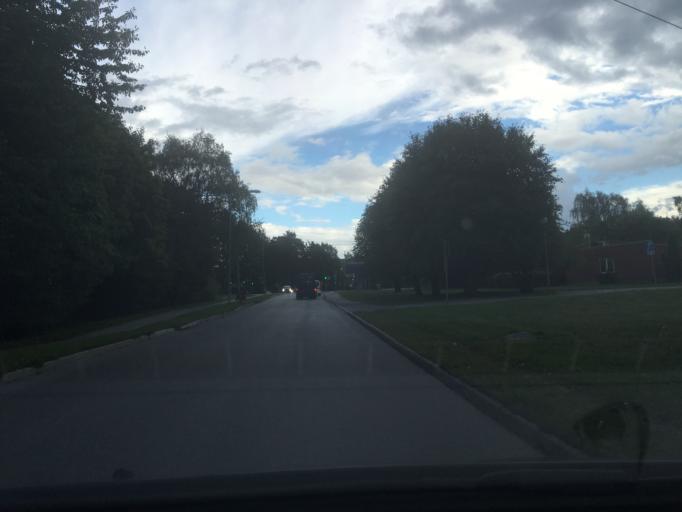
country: SE
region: Stockholm
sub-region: Stockholms Kommun
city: Bromma
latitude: 59.3365
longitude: 17.9287
